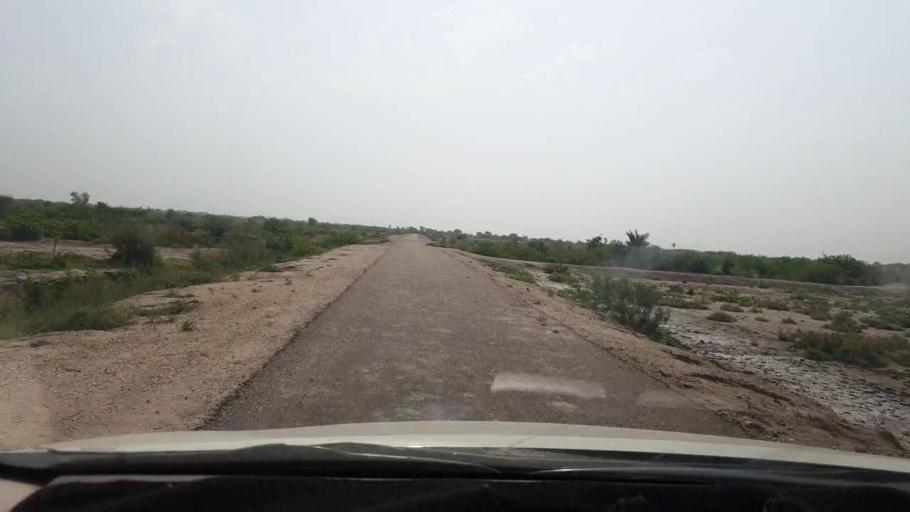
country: PK
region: Sindh
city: Rohri
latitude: 27.6046
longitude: 69.0310
